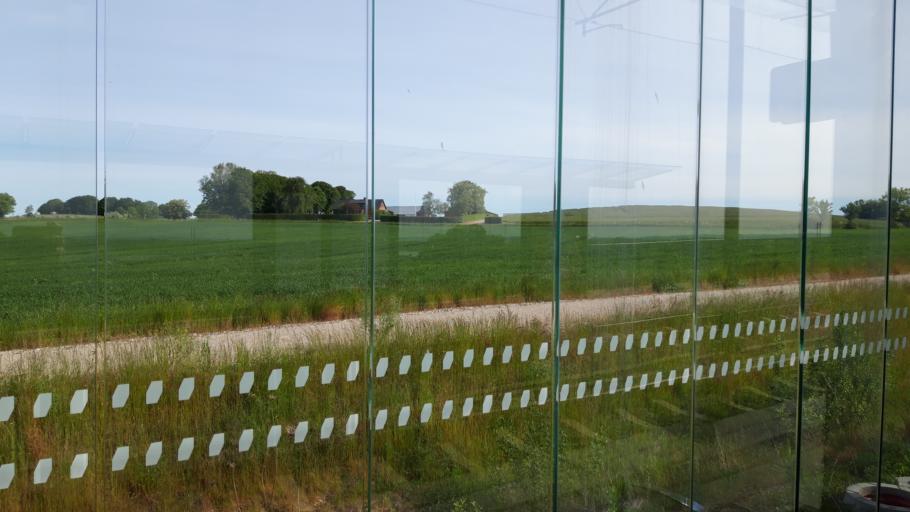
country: DK
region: Central Jutland
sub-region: Arhus Kommune
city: Lystrup
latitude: 56.2272
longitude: 10.2006
